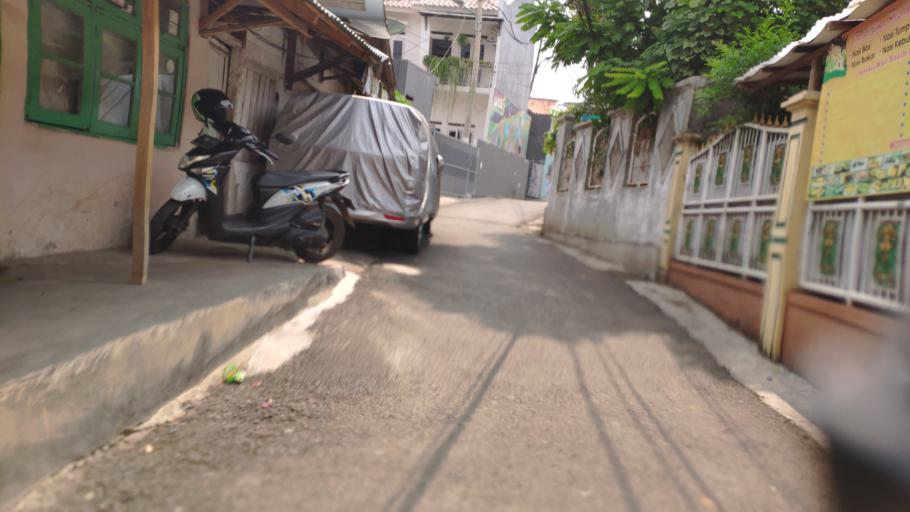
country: ID
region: West Java
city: Depok
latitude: -6.3095
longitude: 106.8355
